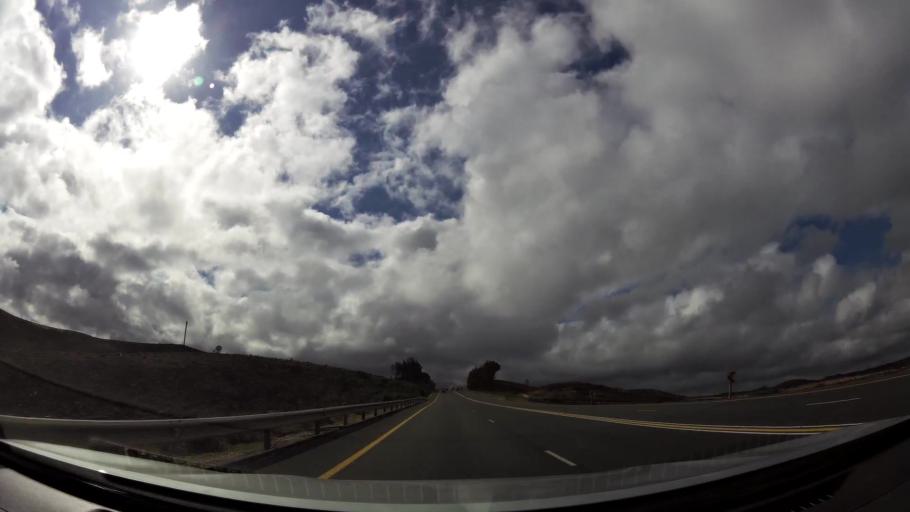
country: ZA
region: Western Cape
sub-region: Eden District Municipality
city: Knysna
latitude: -34.0402
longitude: 23.1196
